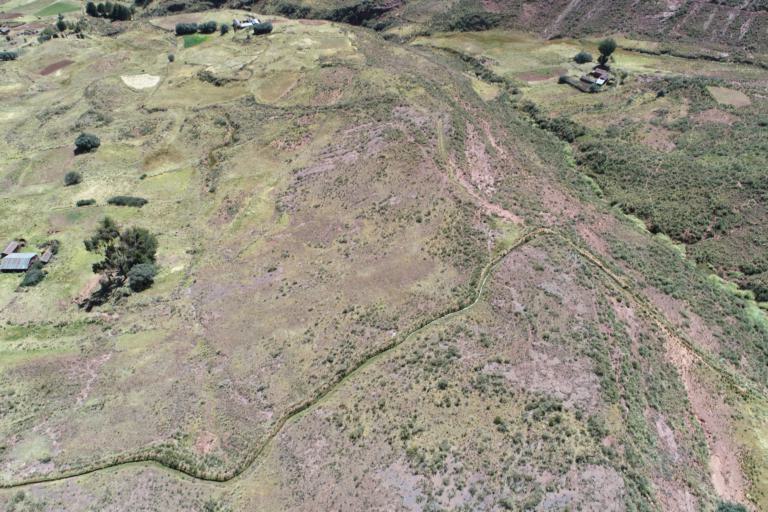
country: BO
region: La Paz
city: Tiahuanaco
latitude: -16.6095
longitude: -68.7610
